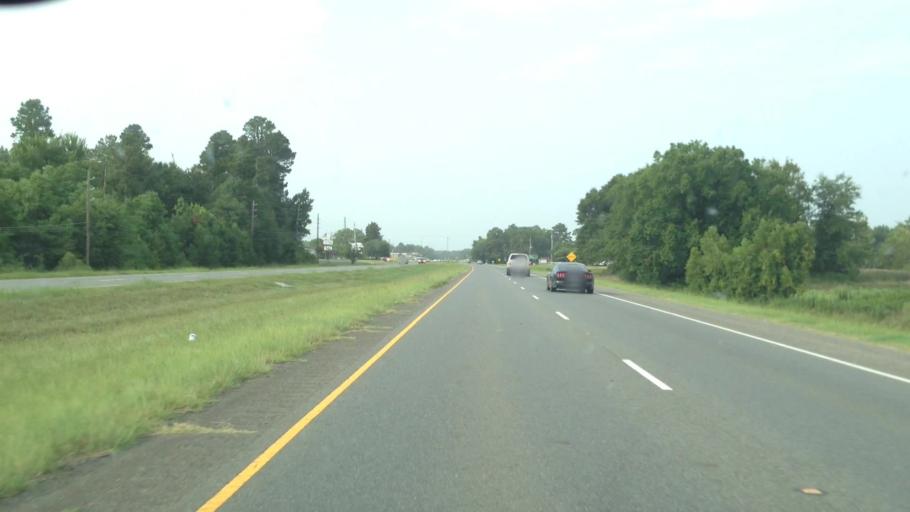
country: US
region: Louisiana
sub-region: De Soto Parish
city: Stonewall
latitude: 32.3742
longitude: -93.8224
